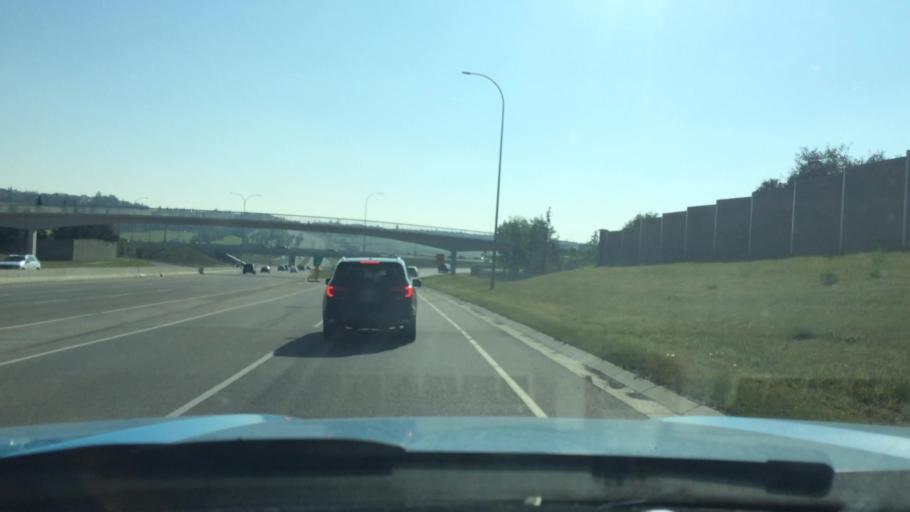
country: CA
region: Alberta
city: Calgary
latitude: 51.1425
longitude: -114.0978
